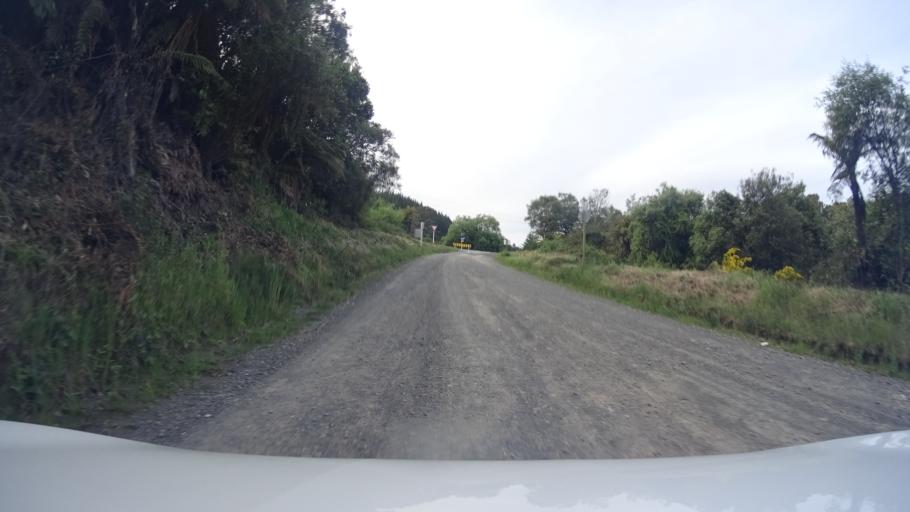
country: NZ
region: Bay of Plenty
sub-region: Rotorua District
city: Rotorua
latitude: -38.3221
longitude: 176.3732
